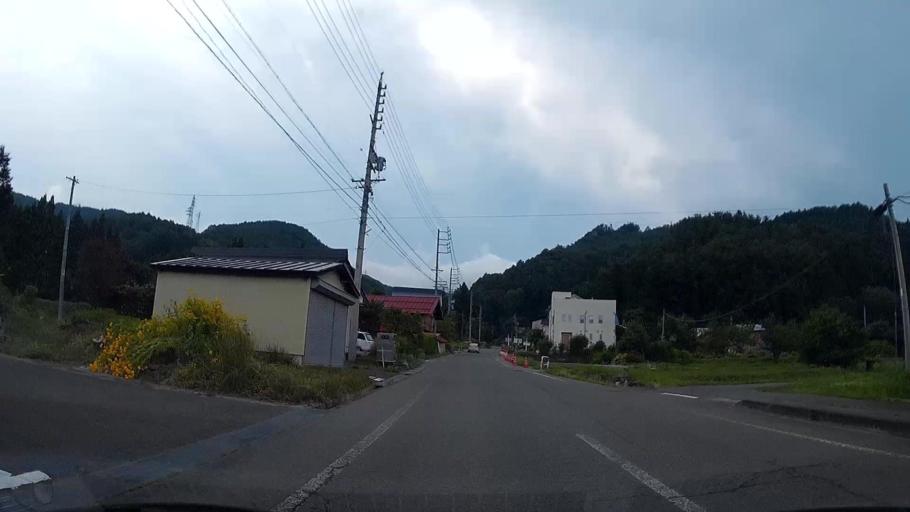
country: JP
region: Nagano
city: Iiyama
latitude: 36.8285
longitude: 138.4190
